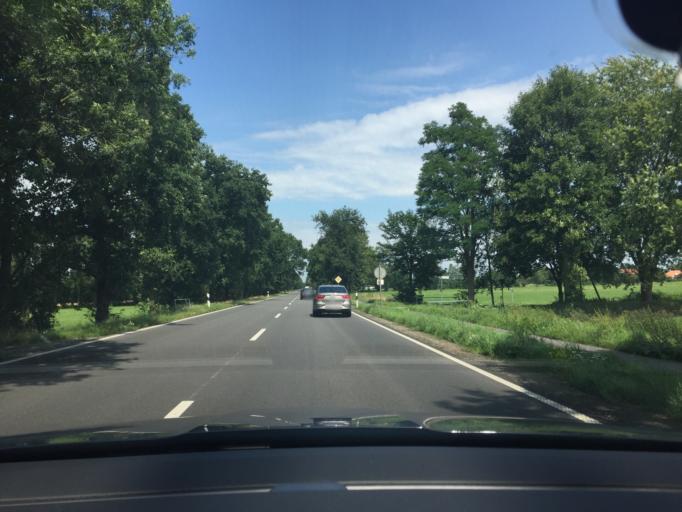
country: DE
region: Lower Saxony
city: Hesel
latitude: 53.3183
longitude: 7.5983
